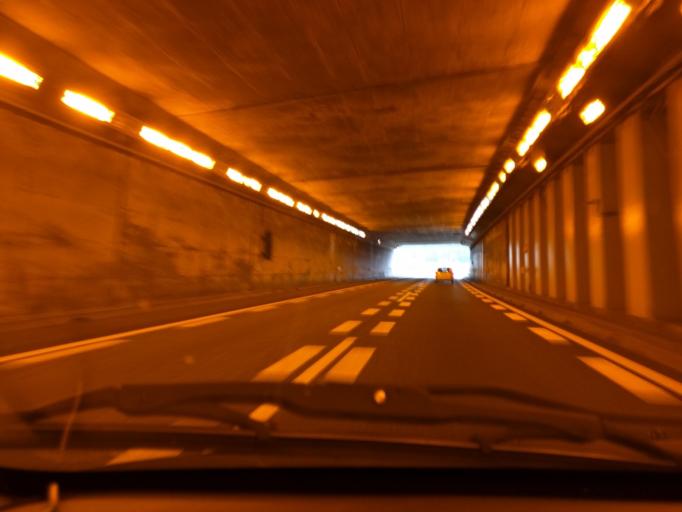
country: JP
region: Niigata
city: Muikamachi
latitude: 37.2311
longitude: 138.9766
